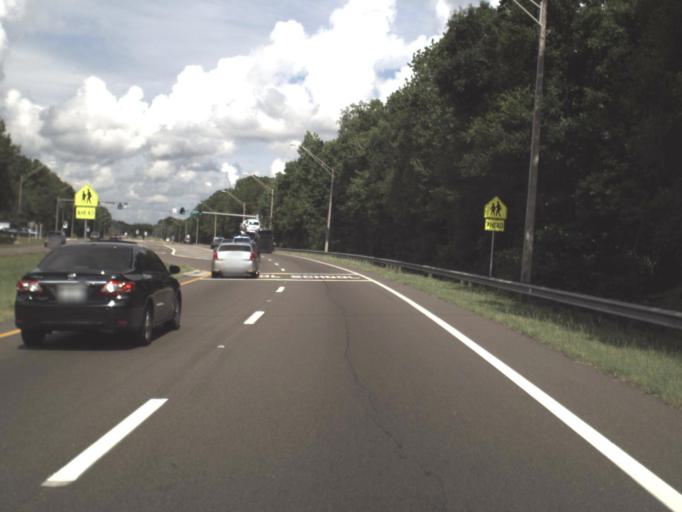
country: US
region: Florida
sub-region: Duval County
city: Jacksonville
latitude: 30.3569
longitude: -81.6845
